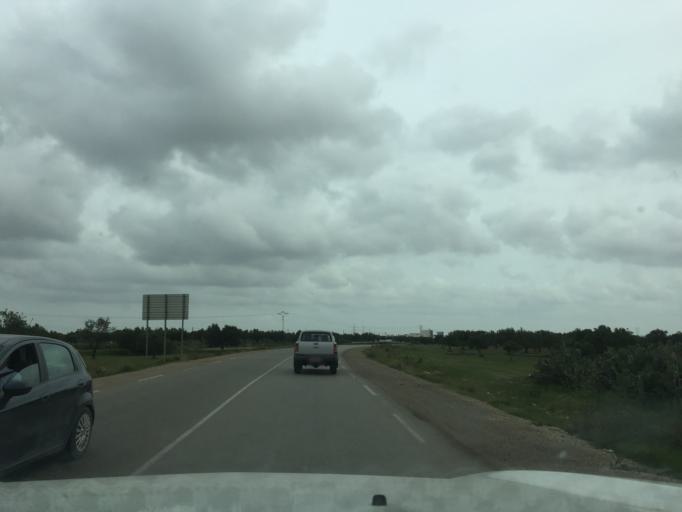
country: TN
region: Al Munastir
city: Manzil Kamil
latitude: 35.6237
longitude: 10.6857
